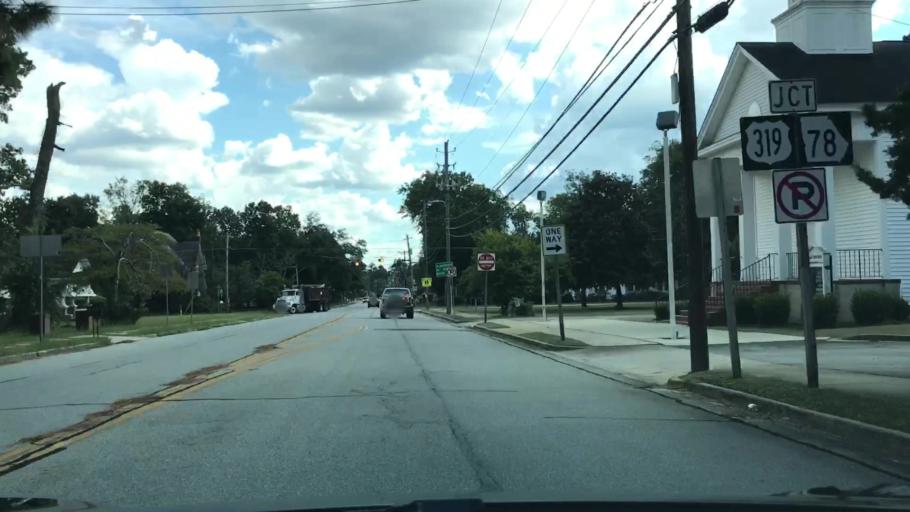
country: US
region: Georgia
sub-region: Jefferson County
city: Wadley
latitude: 32.8673
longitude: -82.4046
